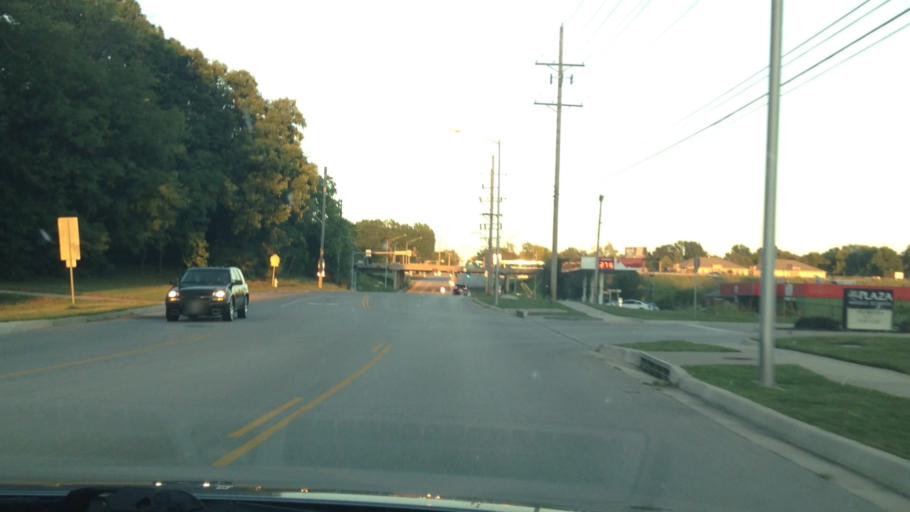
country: US
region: Missouri
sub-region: Platte County
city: Parkville
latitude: 39.2251
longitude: -94.6541
